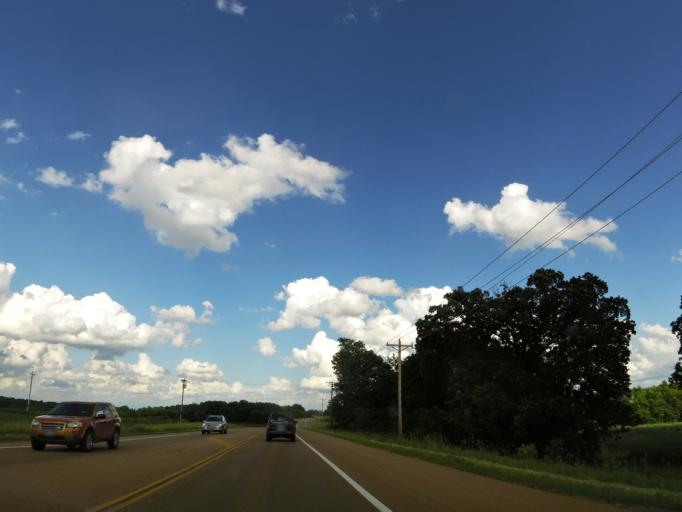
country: US
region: Minnesota
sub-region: Carver County
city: Victoria
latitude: 44.8191
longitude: -93.7051
